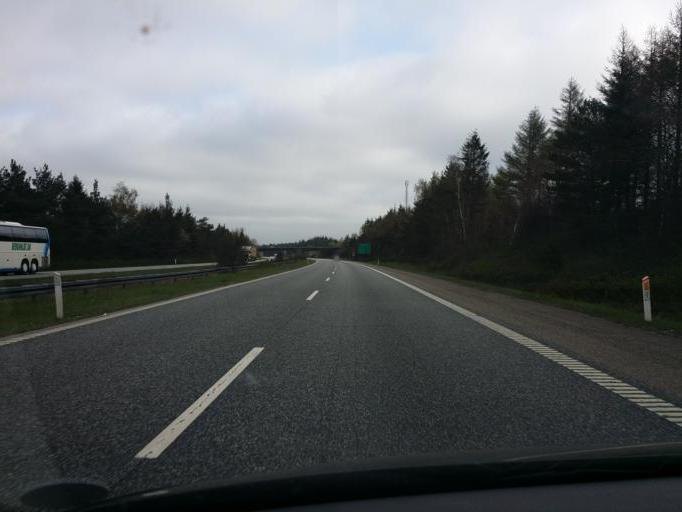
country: DK
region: South Denmark
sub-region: Aabenraa Kommune
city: Krusa
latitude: 54.8717
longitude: 9.3759
